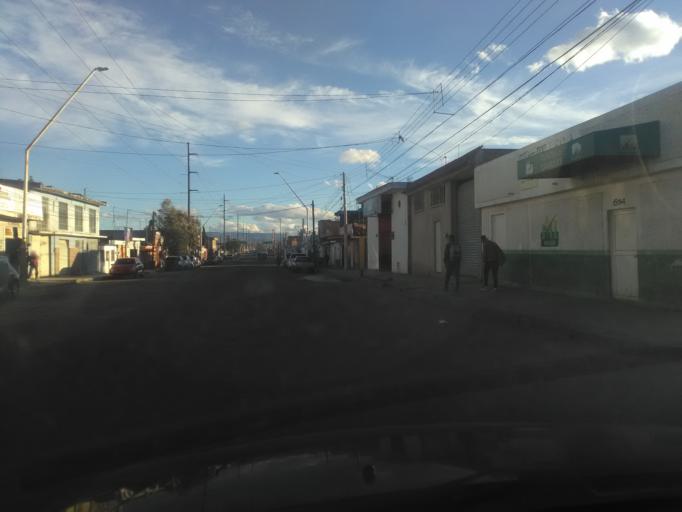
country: MX
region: Durango
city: Victoria de Durango
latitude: 24.0192
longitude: -104.6328
